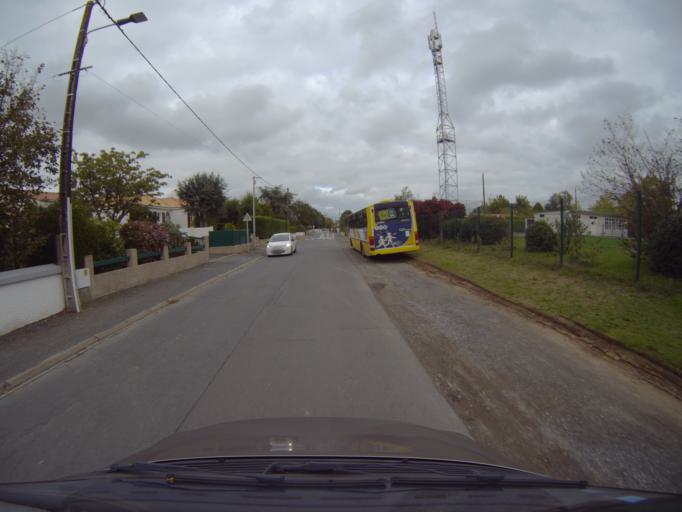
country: FR
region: Pays de la Loire
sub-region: Departement de la Loire-Atlantique
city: Clisson
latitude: 47.0946
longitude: -1.2743
